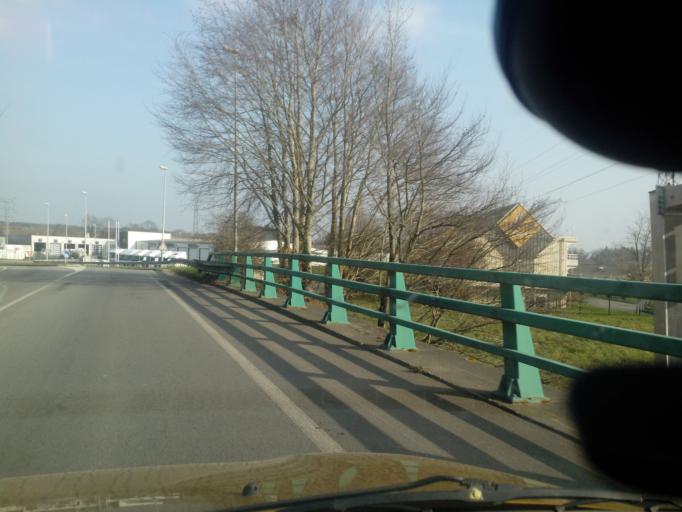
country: FR
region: Brittany
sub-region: Departement du Morbihan
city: Vannes
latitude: 47.6695
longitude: -2.7238
